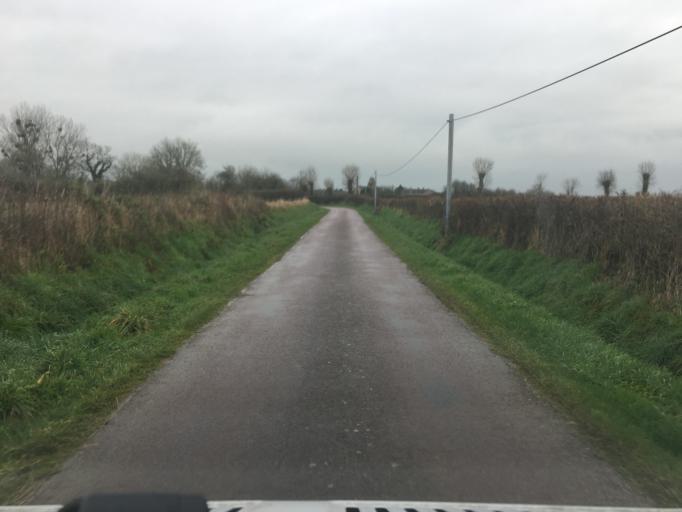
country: FR
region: Lower Normandy
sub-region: Departement de la Manche
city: Sainte-Mere-Eglise
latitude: 49.4325
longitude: -1.2614
